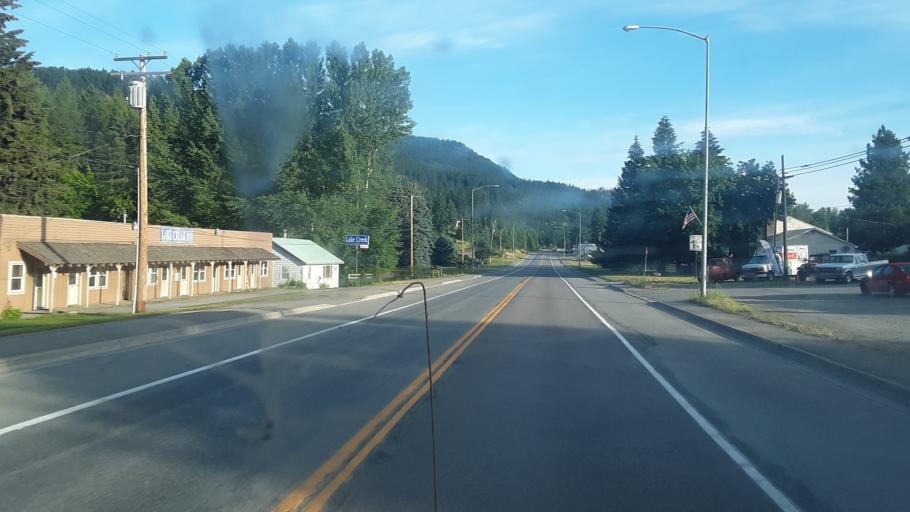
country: US
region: Montana
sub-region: Lincoln County
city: Libby
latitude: 48.4527
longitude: -115.8862
